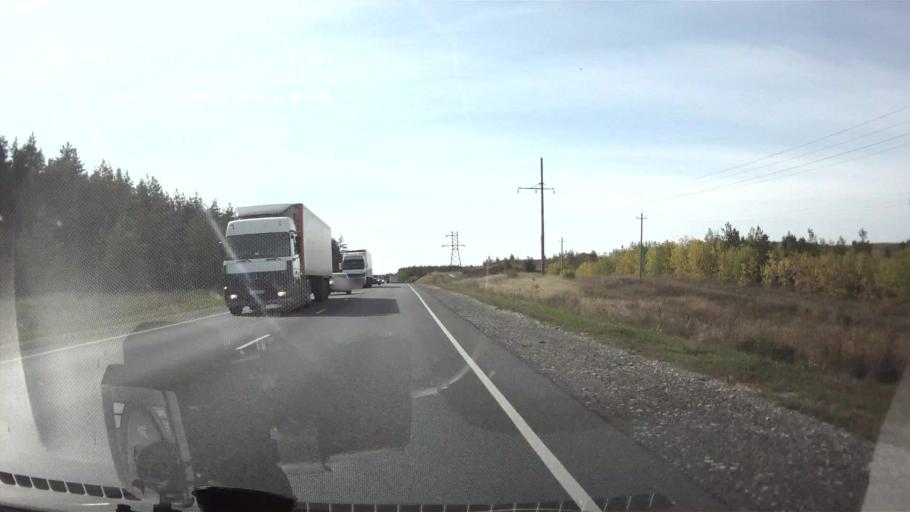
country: RU
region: Saratov
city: Khvalynsk
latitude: 52.5373
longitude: 48.0445
